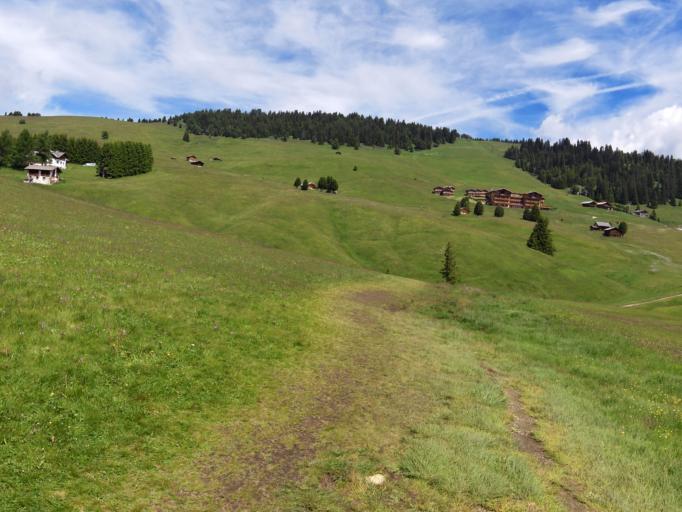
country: IT
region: Trentino-Alto Adige
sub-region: Bolzano
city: Ortisei
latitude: 46.5504
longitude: 11.6586
